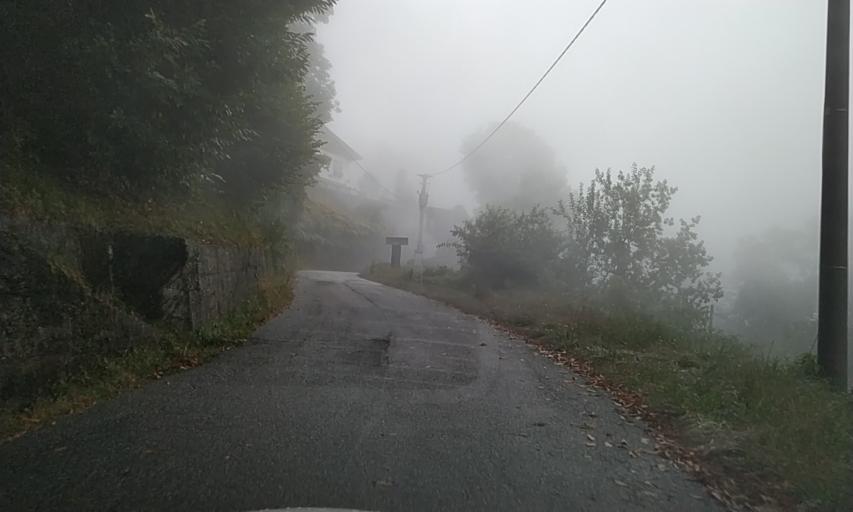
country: IT
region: Piedmont
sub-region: Provincia di Vercelli
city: Civiasco
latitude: 45.8303
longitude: 8.2848
